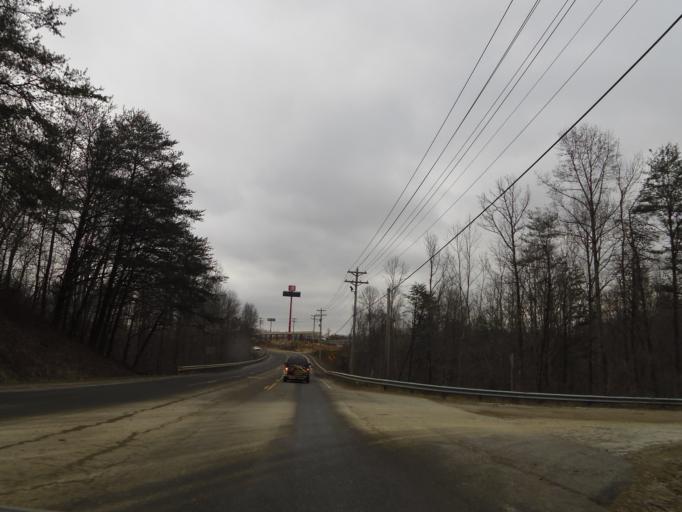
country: US
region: Tennessee
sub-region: Campbell County
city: Jacksboro
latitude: 36.3793
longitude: -84.2508
